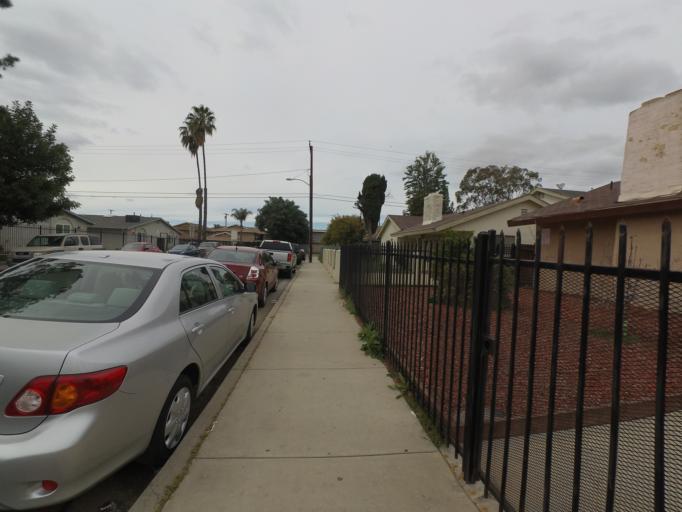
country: US
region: California
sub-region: Riverside County
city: March Air Force Base
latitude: 33.9191
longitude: -117.2644
